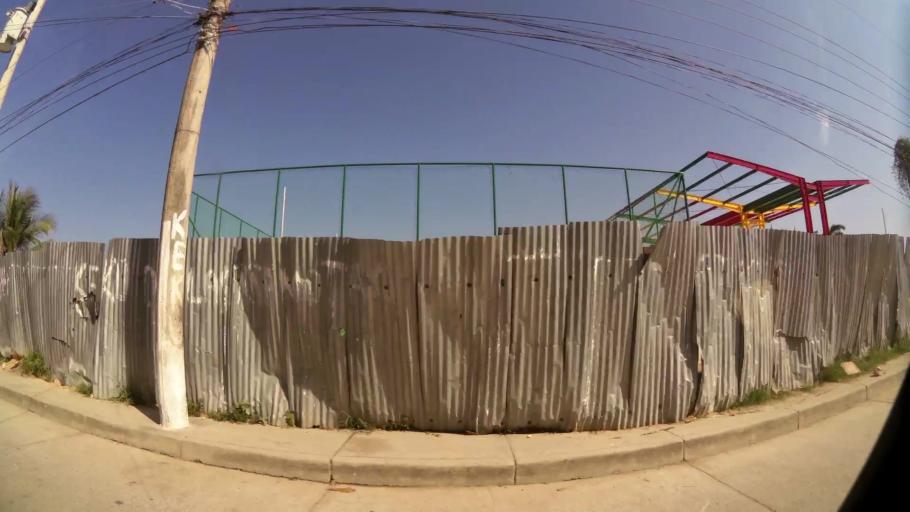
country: CO
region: Bolivar
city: Cartagena
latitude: 10.4137
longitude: -75.5116
